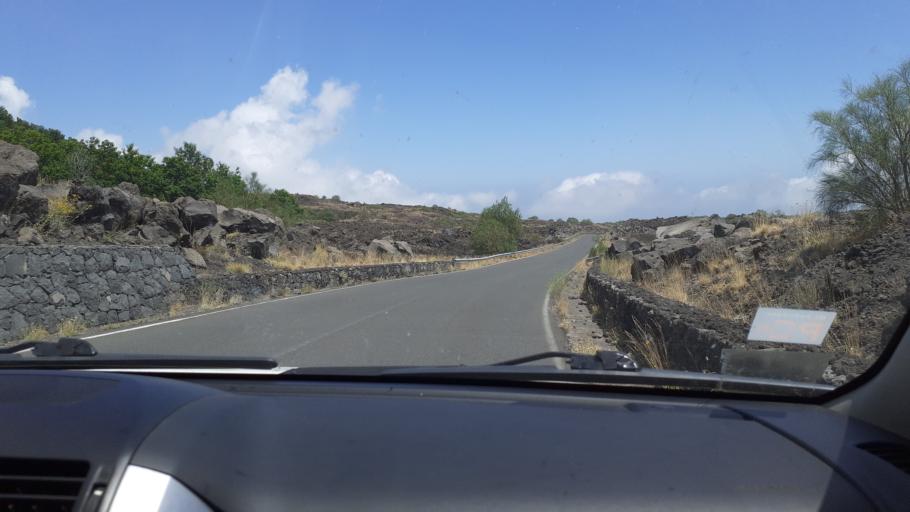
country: IT
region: Sicily
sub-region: Catania
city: Nicolosi
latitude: 37.6876
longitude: 15.0248
